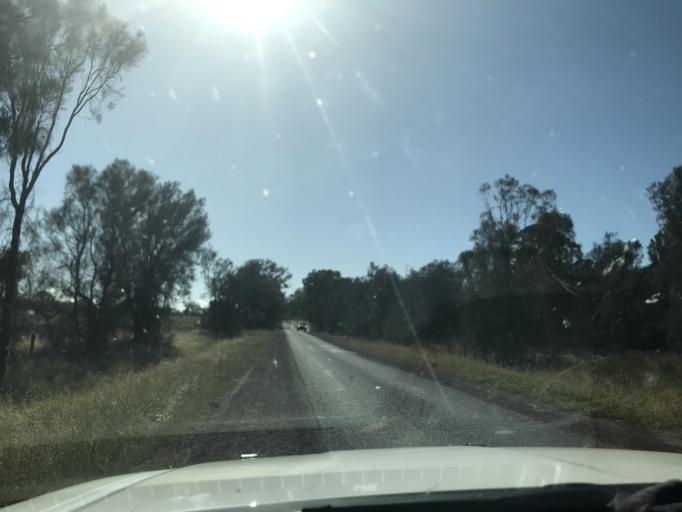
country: AU
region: Victoria
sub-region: Horsham
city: Horsham
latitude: -37.0069
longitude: 141.6401
